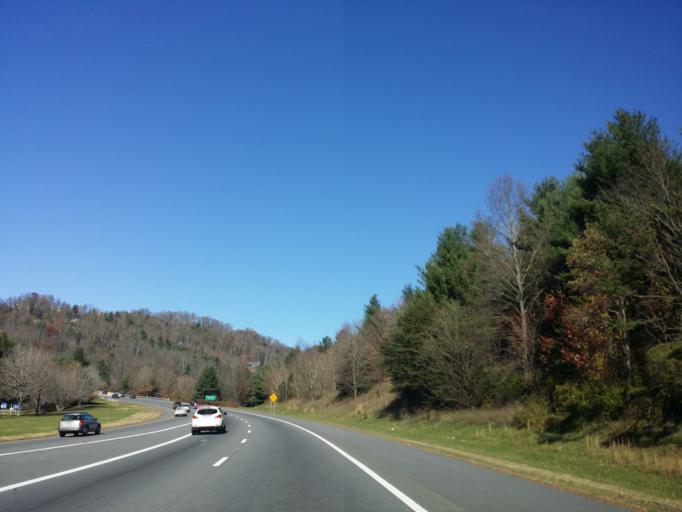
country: US
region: North Carolina
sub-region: Buncombe County
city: Asheville
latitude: 35.5965
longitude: -82.5286
